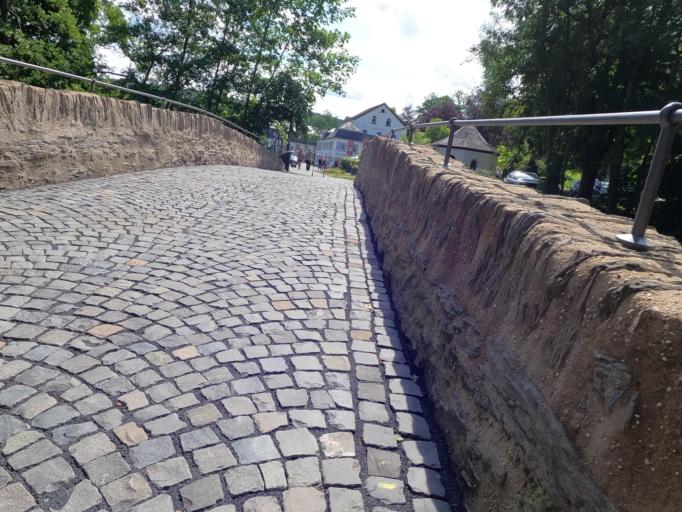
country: DE
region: Rheinland-Pfalz
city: Limbach
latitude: 50.6852
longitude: 7.7983
